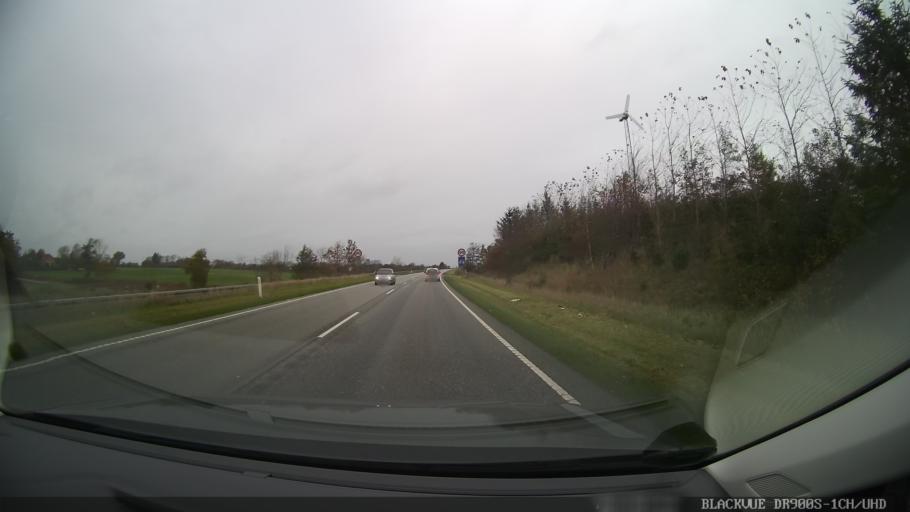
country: DK
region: North Denmark
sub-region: Thisted Kommune
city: Thisted
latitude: 56.8384
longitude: 8.7035
